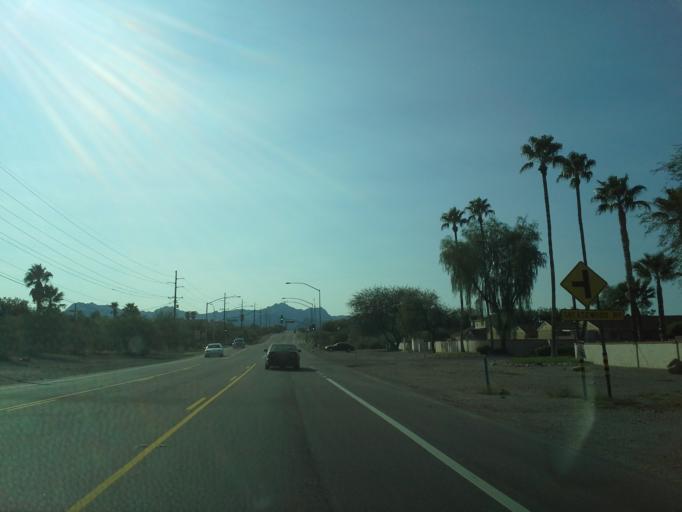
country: US
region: Arizona
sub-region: Pima County
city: Flowing Wells
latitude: 32.2507
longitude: -111.0186
